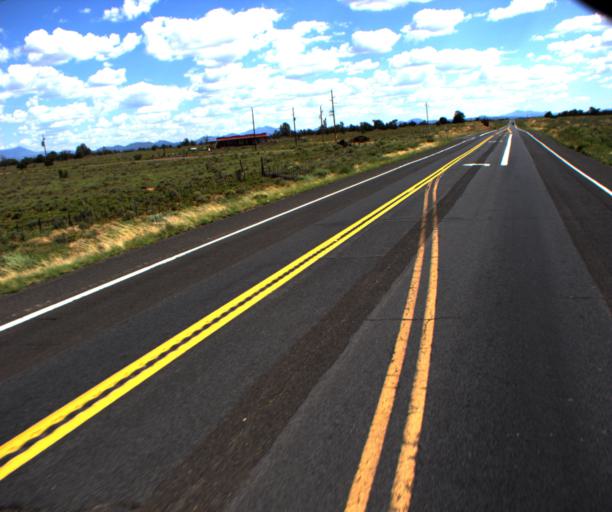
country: US
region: Arizona
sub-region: Coconino County
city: Grand Canyon Village
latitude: 35.7053
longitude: -112.1323
